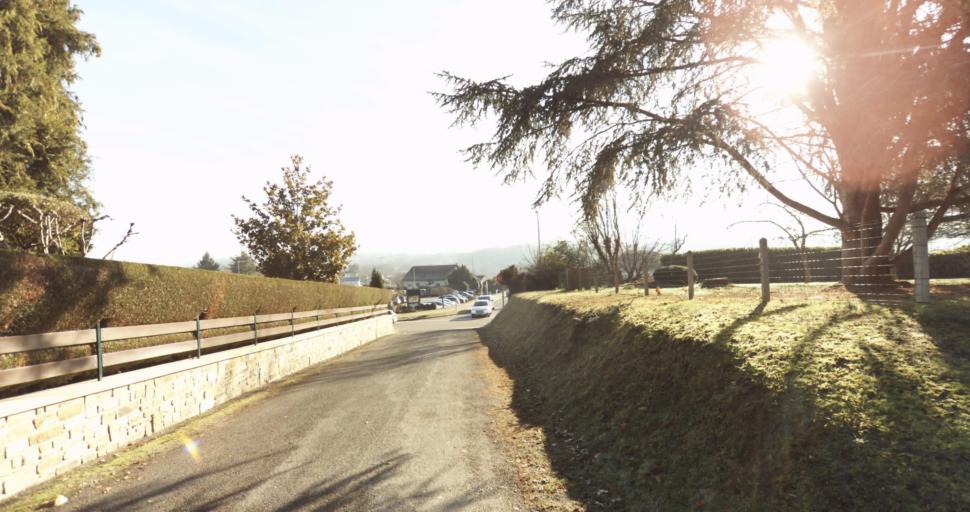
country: FR
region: Limousin
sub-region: Departement de la Haute-Vienne
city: Aixe-sur-Vienne
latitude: 45.8026
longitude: 1.1506
